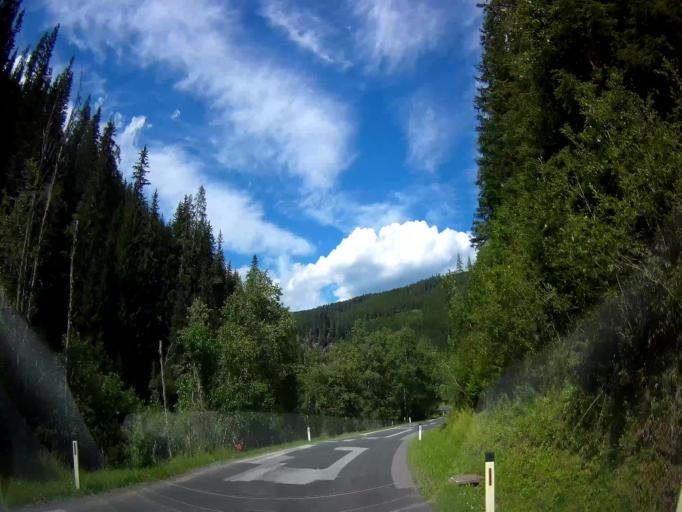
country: AT
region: Styria
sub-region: Politischer Bezirk Murau
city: Stadl an der Mur
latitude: 47.0247
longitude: 14.0061
